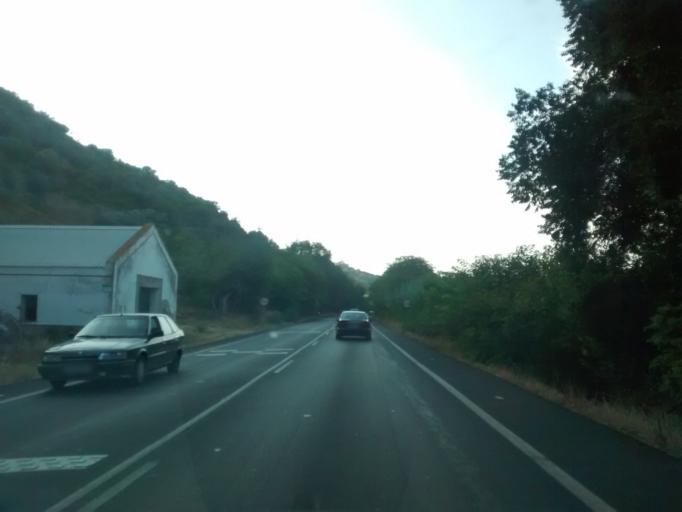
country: ES
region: Andalusia
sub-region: Provincia de Cadiz
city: Vejer de la Frontera
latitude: 36.2547
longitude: -5.9579
